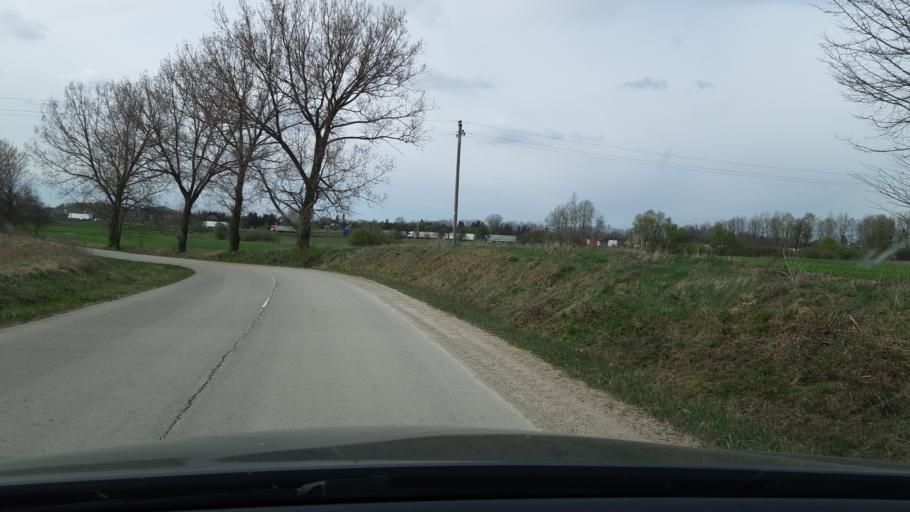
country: LT
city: Virbalis
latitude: 54.6221
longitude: 22.8363
